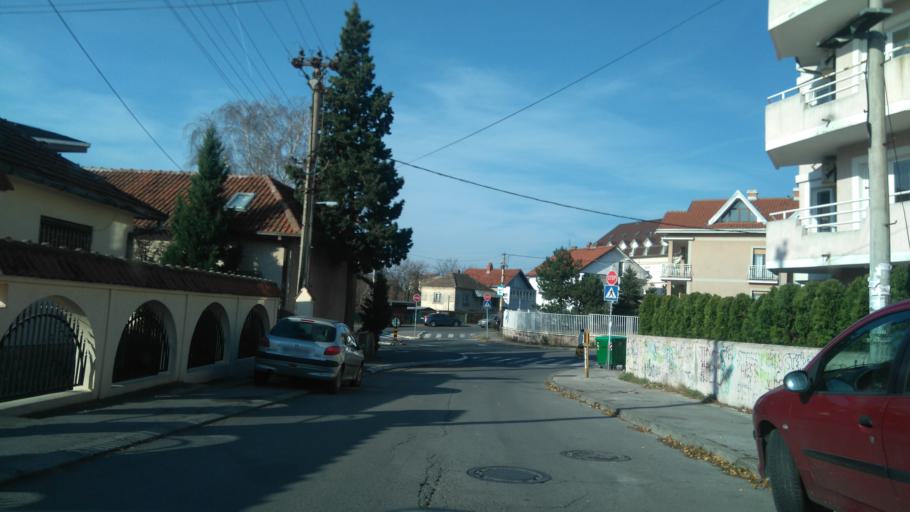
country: RS
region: Central Serbia
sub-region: Belgrade
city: Cukarica
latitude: 44.7590
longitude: 20.4070
